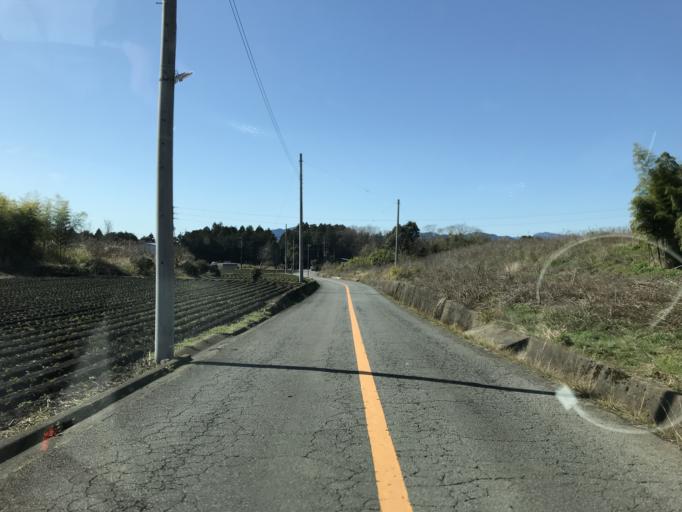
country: JP
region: Shizuoka
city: Fujinomiya
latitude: 35.2353
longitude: 138.6536
